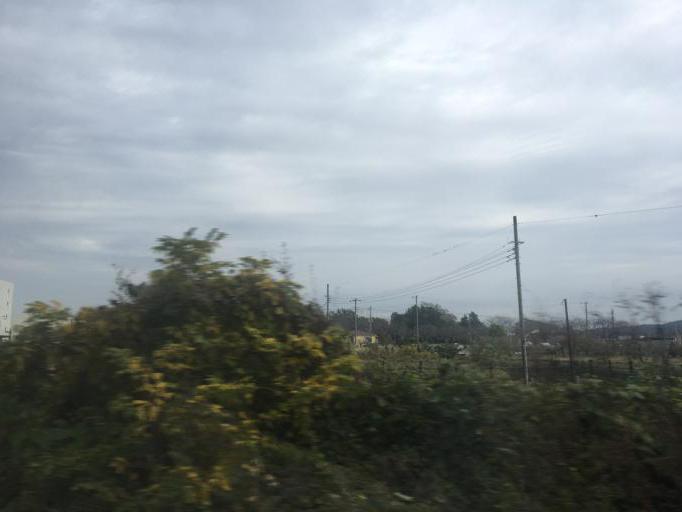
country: JP
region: Tokyo
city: Fussa
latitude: 35.7818
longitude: 139.3432
